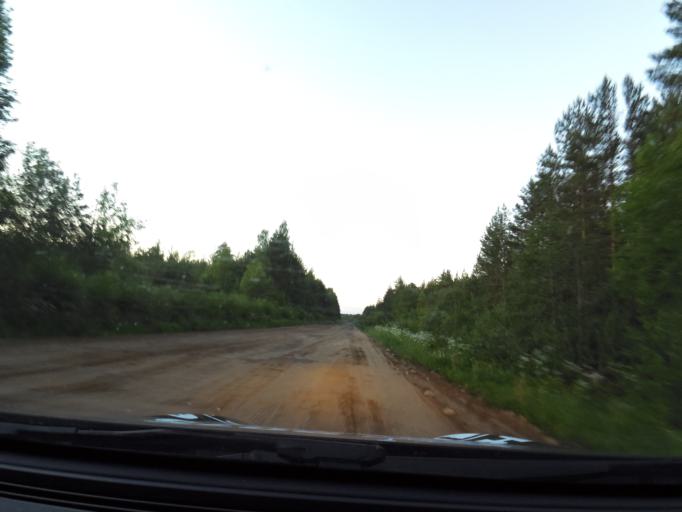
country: RU
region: Leningrad
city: Voznesen'ye
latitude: 60.8628
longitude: 35.9467
